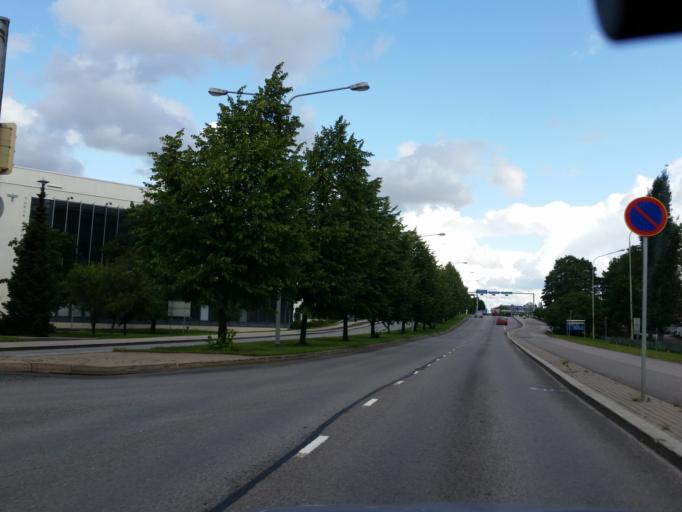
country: FI
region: Varsinais-Suomi
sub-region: Turku
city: Turku
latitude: 60.4538
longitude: 22.2883
